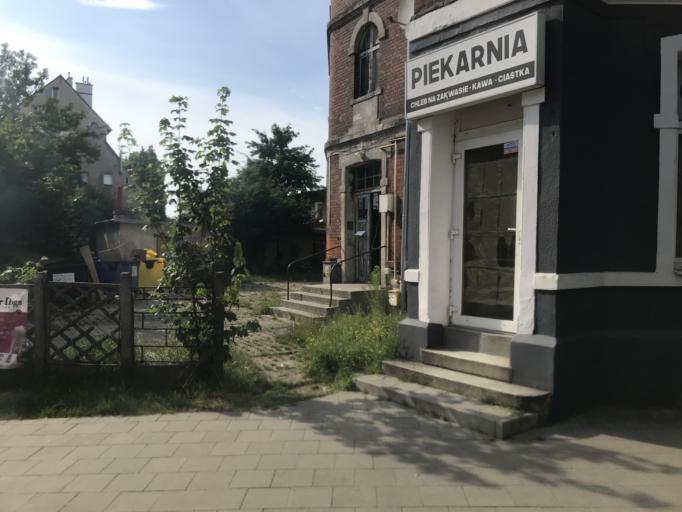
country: PL
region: Pomeranian Voivodeship
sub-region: Gdansk
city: Gdansk
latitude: 54.4057
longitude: 18.6360
